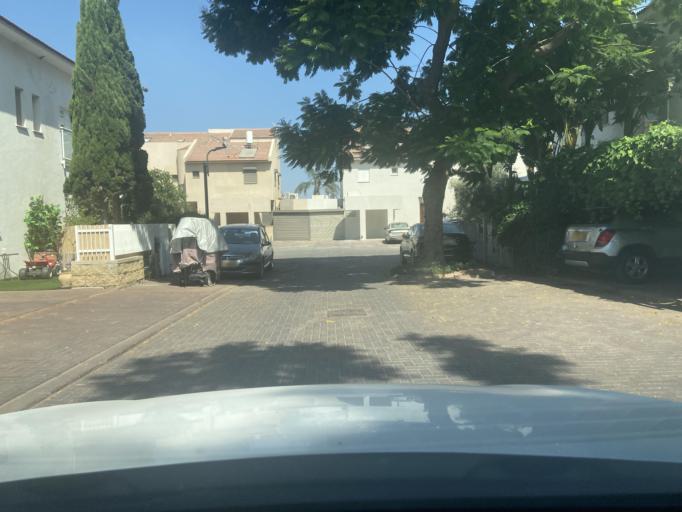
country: IL
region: Central District
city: Yehud
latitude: 32.0338
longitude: 34.8771
